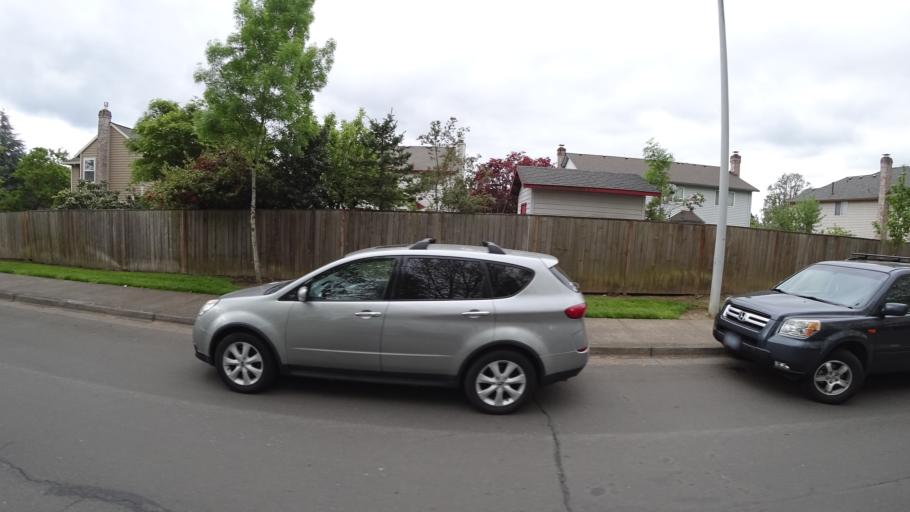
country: US
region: Oregon
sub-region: Washington County
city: Hillsboro
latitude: 45.5429
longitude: -122.9814
